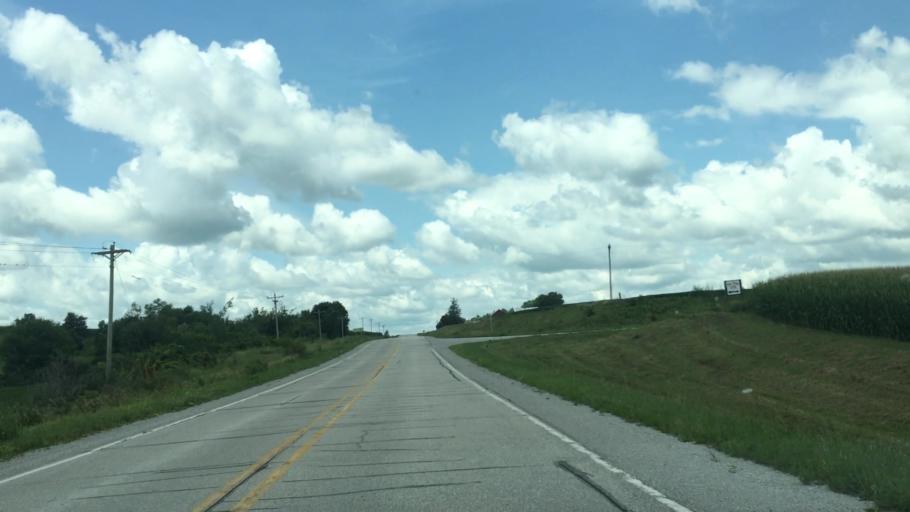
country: US
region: Iowa
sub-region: Johnson County
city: Solon
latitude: 41.8310
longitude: -91.4629
